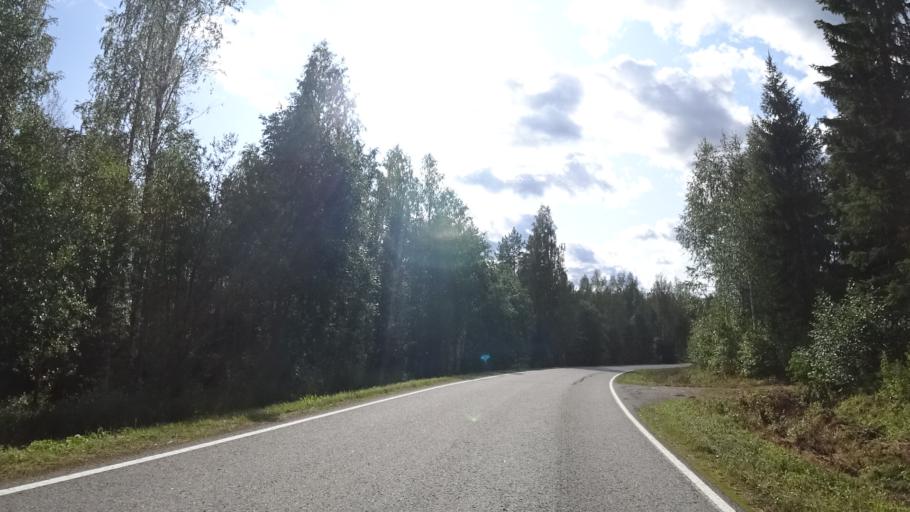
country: RU
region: Republic of Karelia
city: Vyartsilya
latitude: 62.2695
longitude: 30.7992
